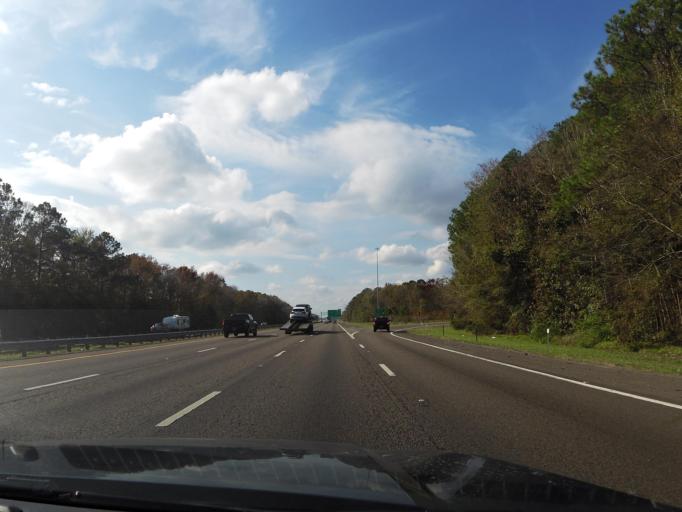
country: US
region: Florida
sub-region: Duval County
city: Baldwin
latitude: 30.3095
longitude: -81.8501
